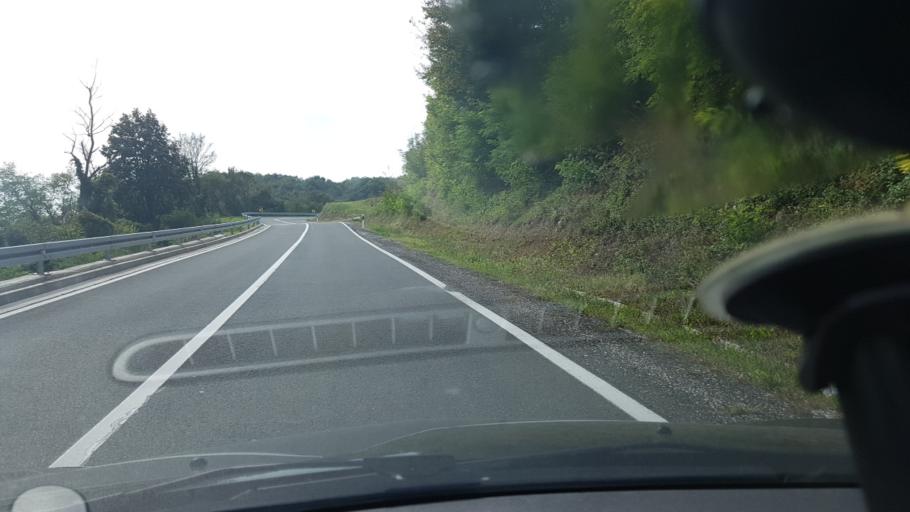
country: HR
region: Varazdinska
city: Ljubescica
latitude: 46.1166
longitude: 16.3576
